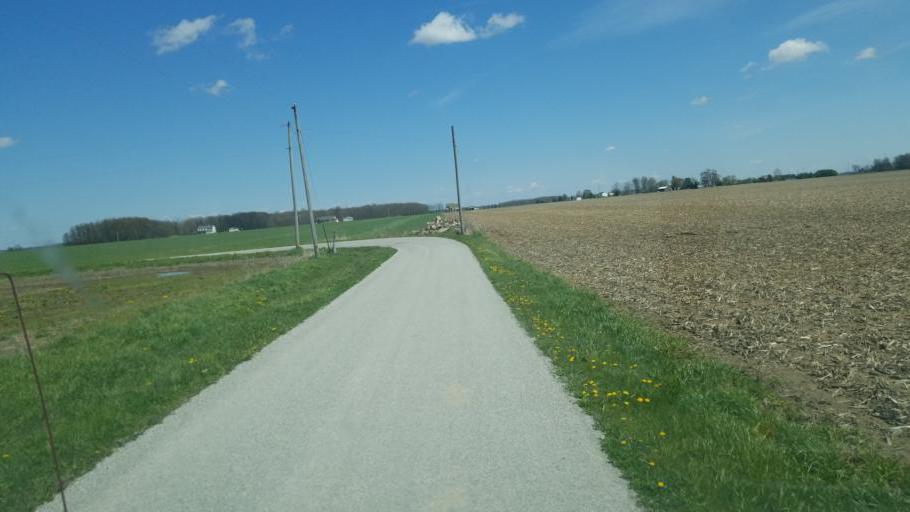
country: US
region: Ohio
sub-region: Marion County
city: Prospect
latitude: 40.3929
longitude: -83.1265
